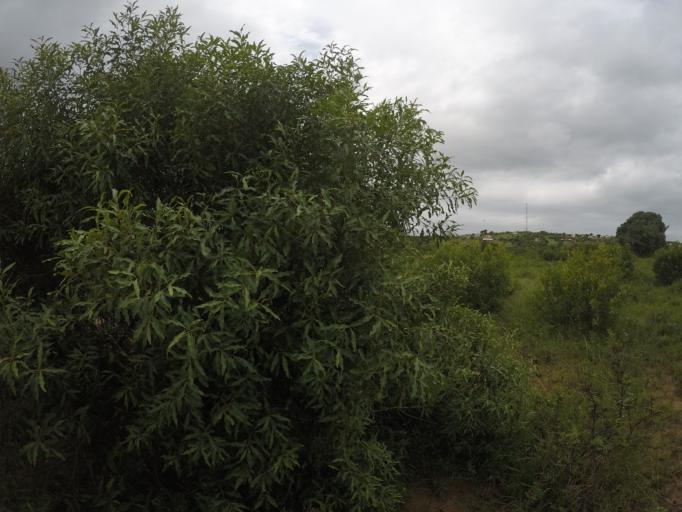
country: ZA
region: KwaZulu-Natal
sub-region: uThungulu District Municipality
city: Empangeni
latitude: -28.6021
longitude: 31.8298
